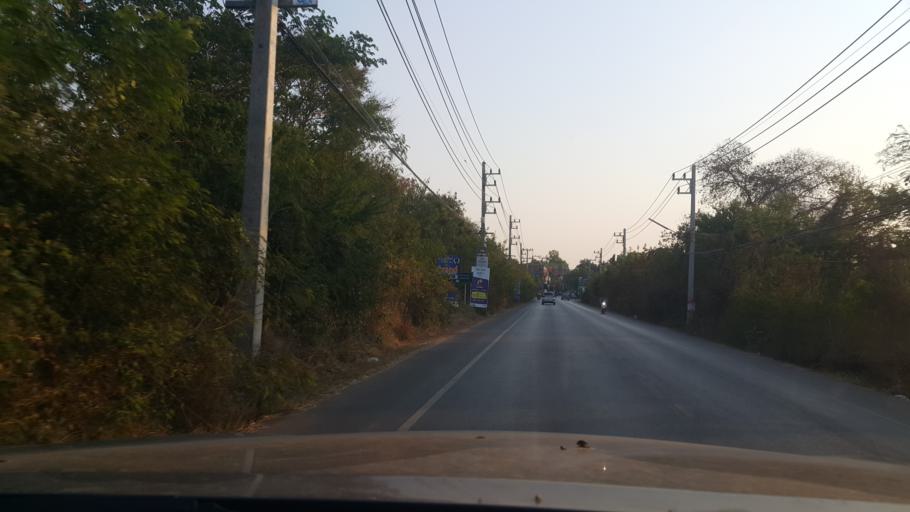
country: TH
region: Nakhon Ratchasima
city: Nakhon Ratchasima
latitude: 14.9397
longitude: 102.0283
